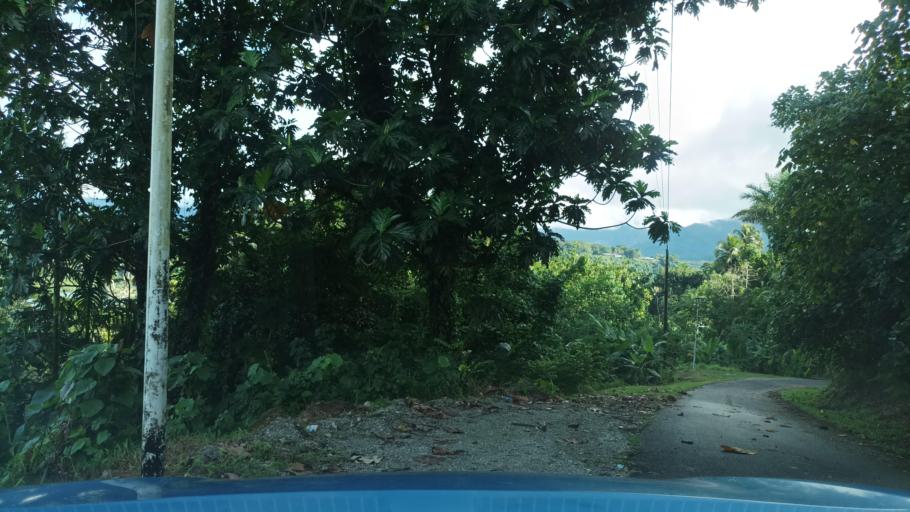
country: FM
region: Pohnpei
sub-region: Kolonia Municipality
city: Kolonia Town
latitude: 6.9651
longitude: 158.1935
